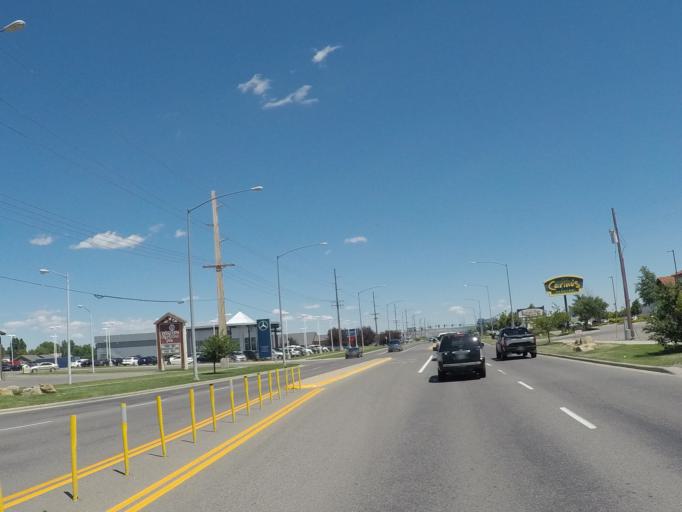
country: US
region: Montana
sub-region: Yellowstone County
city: Billings
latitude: 45.7552
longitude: -108.5953
